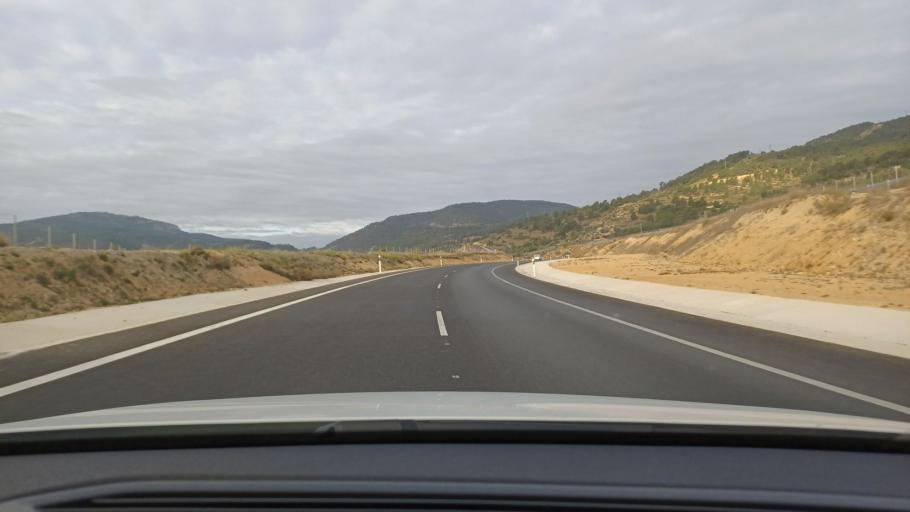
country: ES
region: Valencia
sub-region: Provincia de Valencia
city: La Font de la Figuera
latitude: 38.8302
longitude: -0.8839
